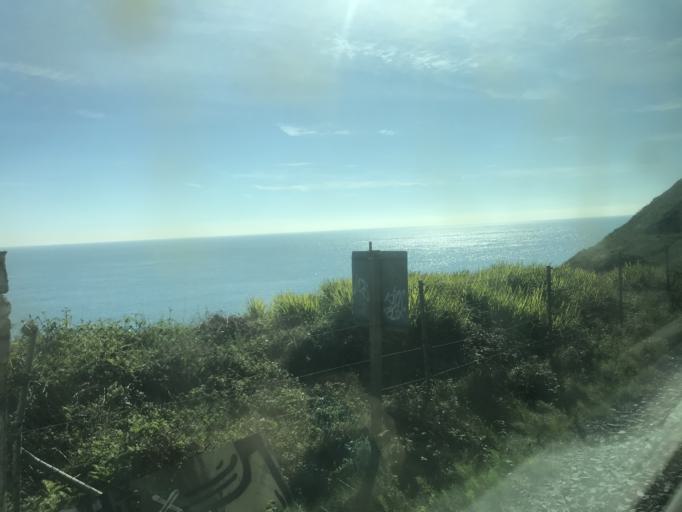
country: IE
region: Leinster
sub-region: Wicklow
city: Bray
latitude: 53.1922
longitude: -6.0809
